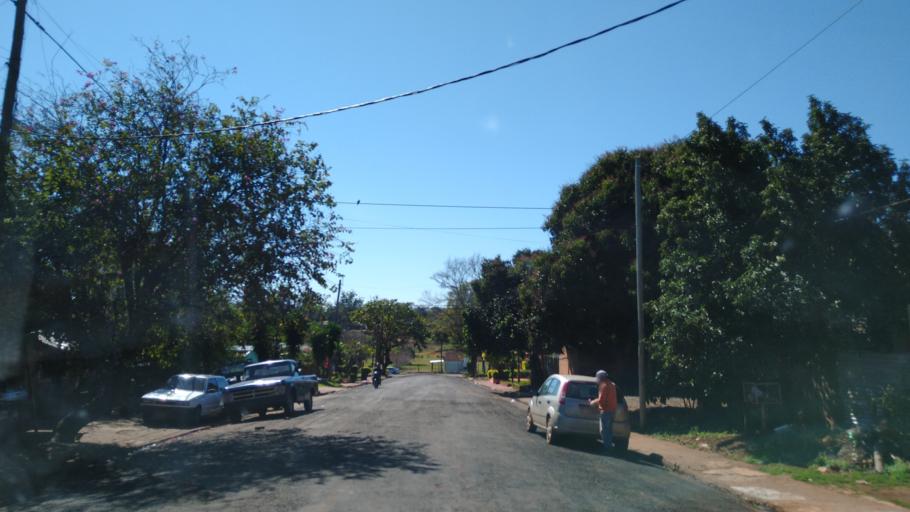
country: AR
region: Misiones
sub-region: Departamento de Capital
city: Posadas
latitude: -27.3953
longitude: -55.9337
